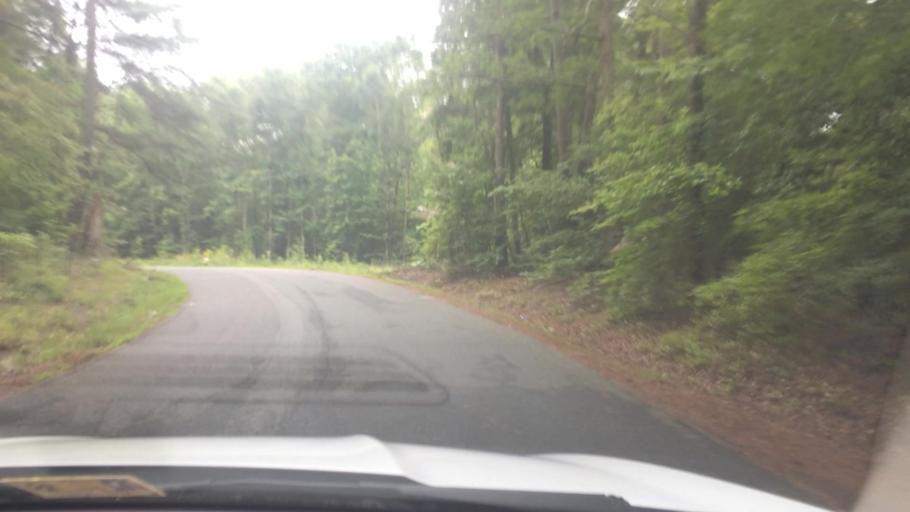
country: US
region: Virginia
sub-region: York County
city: Yorktown
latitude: 37.2204
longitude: -76.5485
